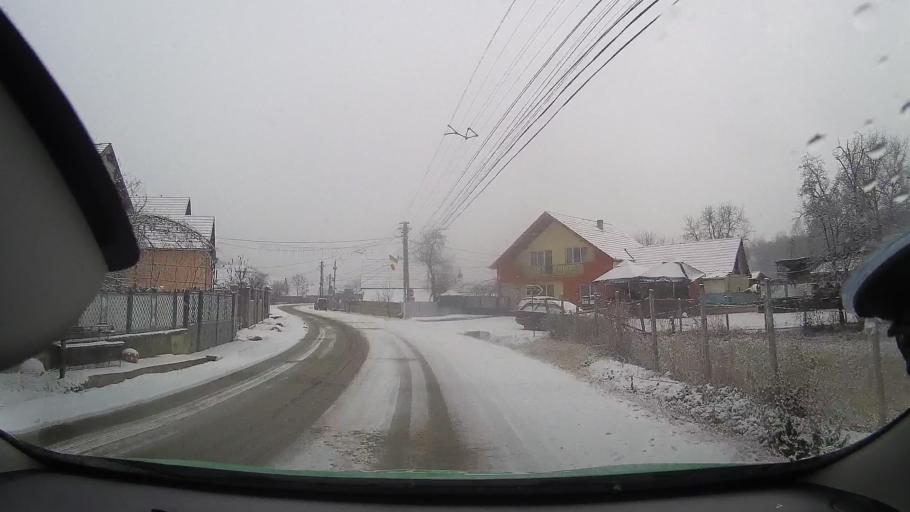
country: RO
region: Alba
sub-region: Comuna Livezile
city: Livezile
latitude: 46.3473
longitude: 23.6407
